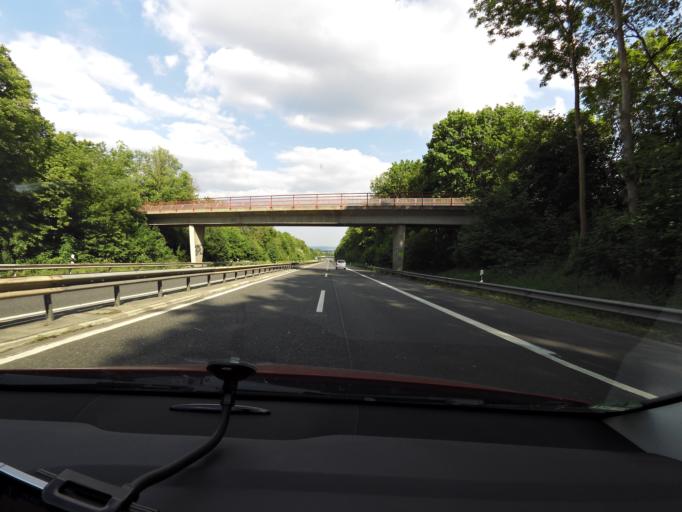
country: DE
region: Rheinland-Pfalz
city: Andernach
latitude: 50.4224
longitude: 7.3978
